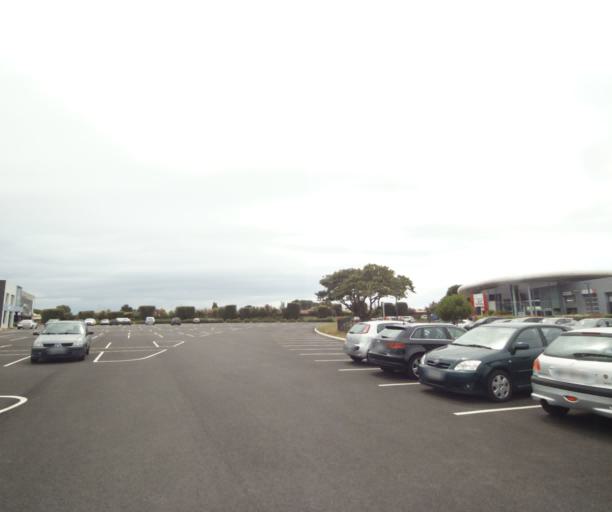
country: FR
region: Pays de la Loire
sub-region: Departement de la Vendee
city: Chateau-d'Olonne
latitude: 46.4987
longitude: -1.7535
